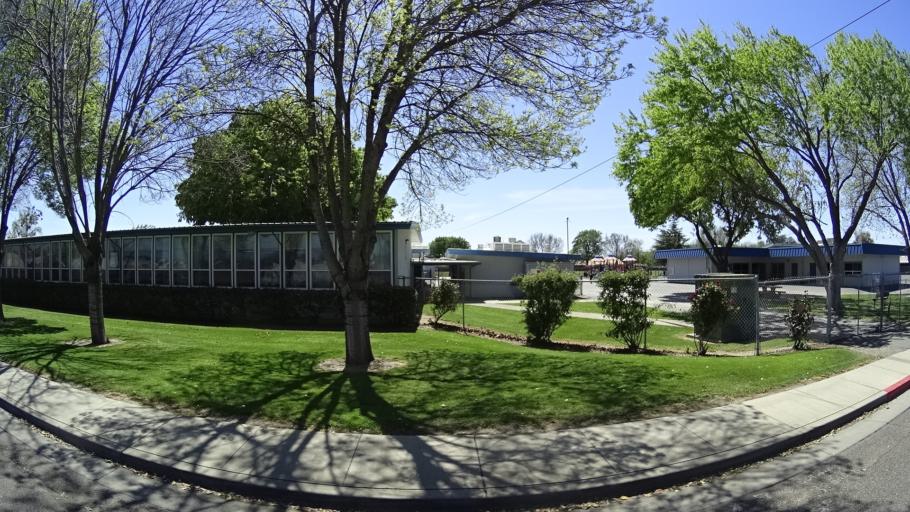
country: US
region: California
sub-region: Glenn County
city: Orland
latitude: 39.7401
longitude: -122.1841
